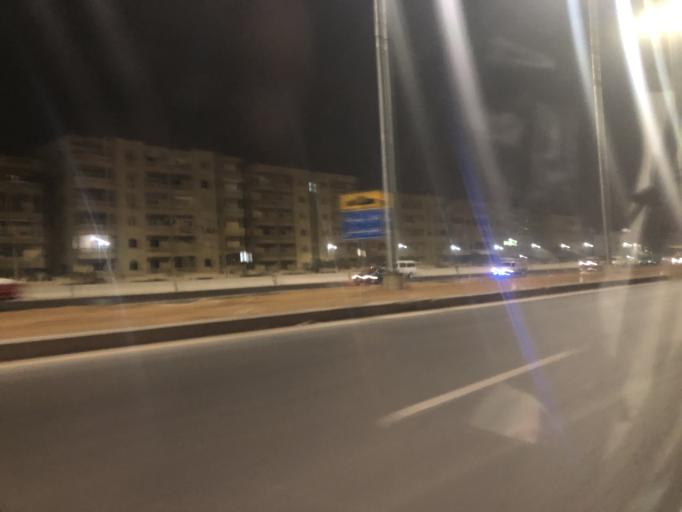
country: EG
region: Al Jizah
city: Al Jizah
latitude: 29.9756
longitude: 31.1113
